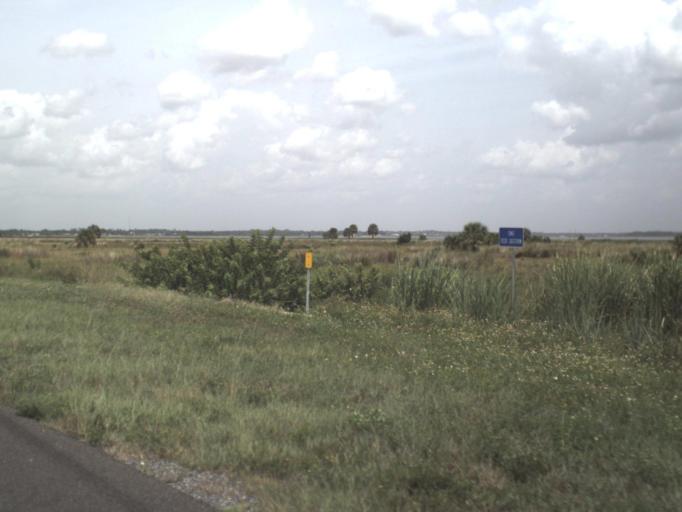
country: US
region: Florida
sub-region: Polk County
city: Crooked Lake Park
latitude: 27.7993
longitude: -81.5972
